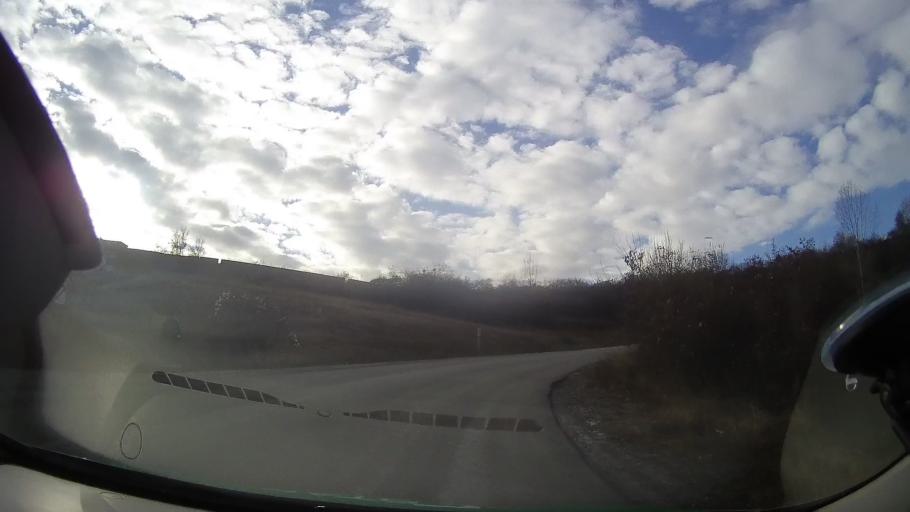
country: RO
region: Cluj
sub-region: Comuna Savadisla
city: Savadisla
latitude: 46.6578
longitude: 23.4510
